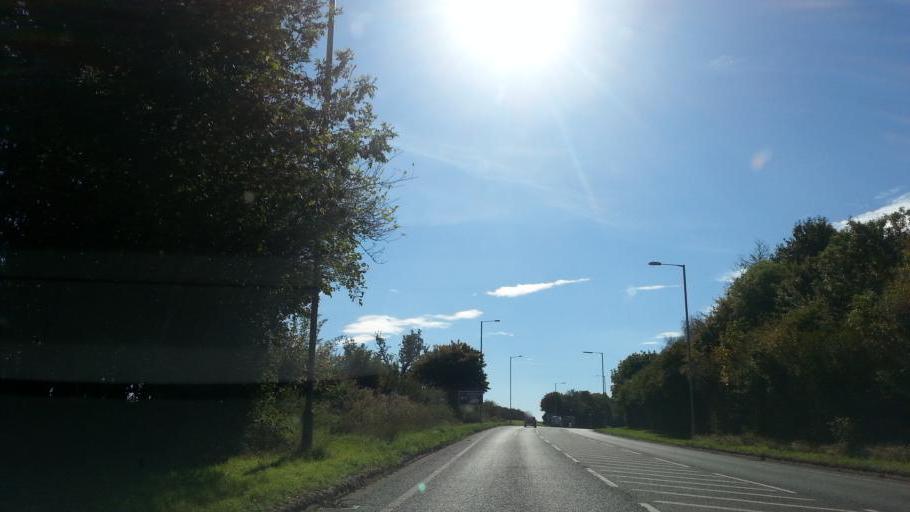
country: GB
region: England
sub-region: Telford and Wrekin
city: Newport
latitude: 52.7573
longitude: -2.3726
